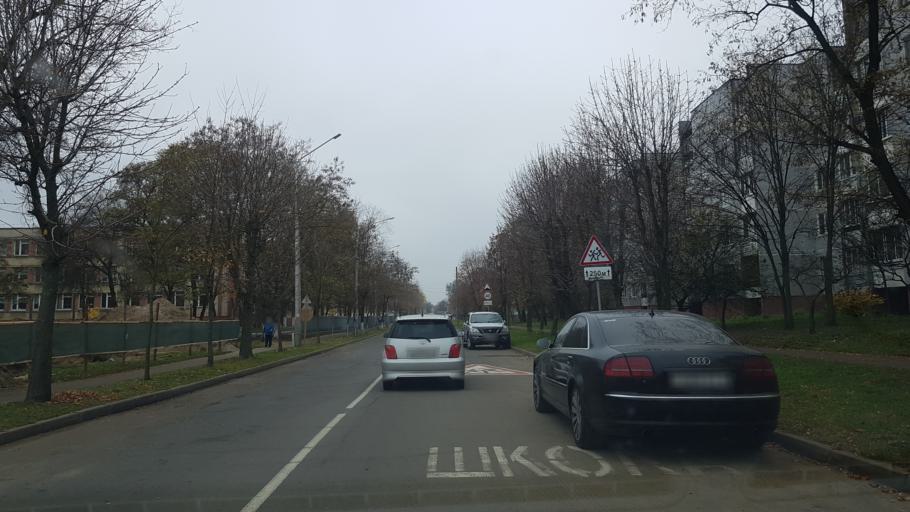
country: BY
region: Mogilev
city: Babruysk
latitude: 53.1516
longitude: 29.2428
